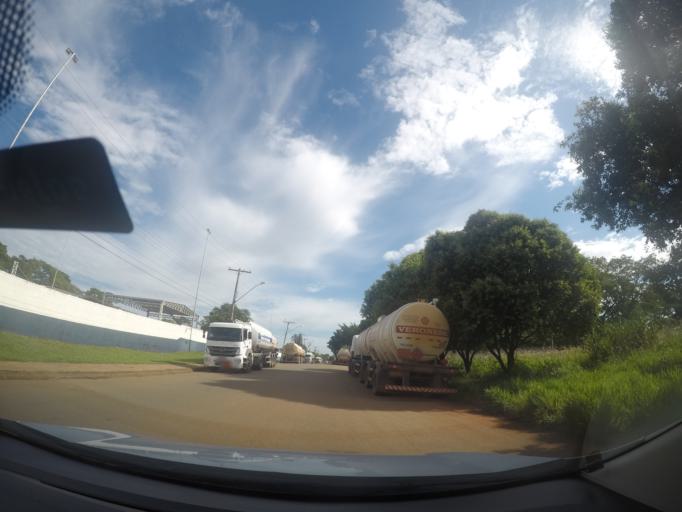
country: BR
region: Goias
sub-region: Goiania
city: Goiania
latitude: -16.6729
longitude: -49.2001
